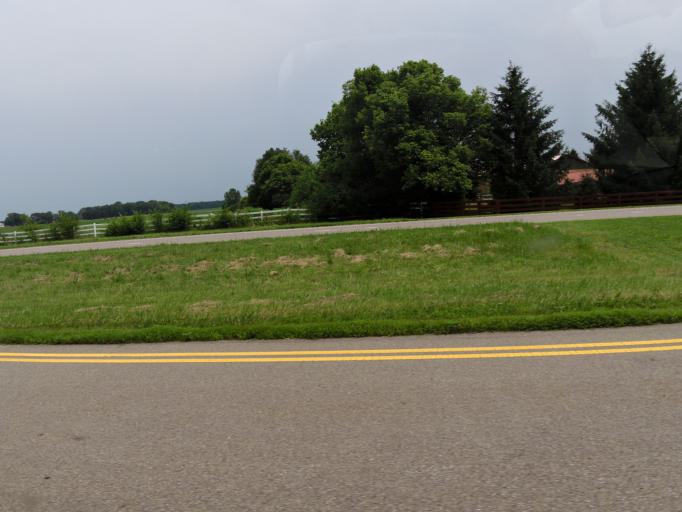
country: US
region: Ohio
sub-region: Greene County
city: Bellbrook
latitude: 39.6154
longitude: -83.9972
